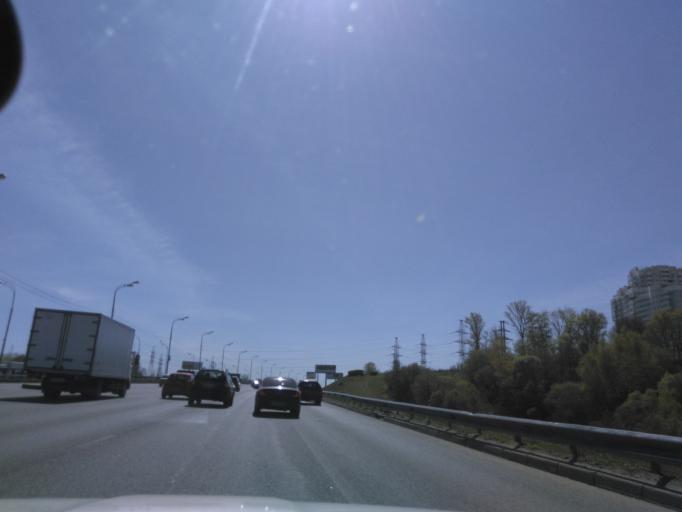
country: RU
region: Moscow
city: Strogino
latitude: 55.8412
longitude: 37.3942
